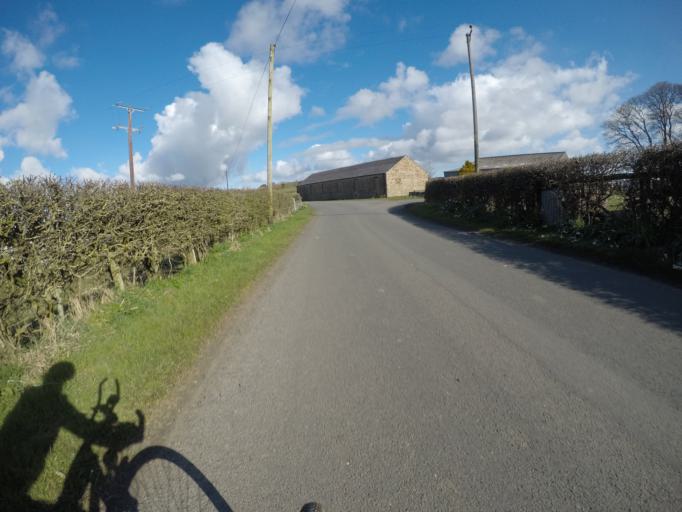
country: GB
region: Scotland
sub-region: North Ayrshire
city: Irvine
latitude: 55.6552
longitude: -4.6531
